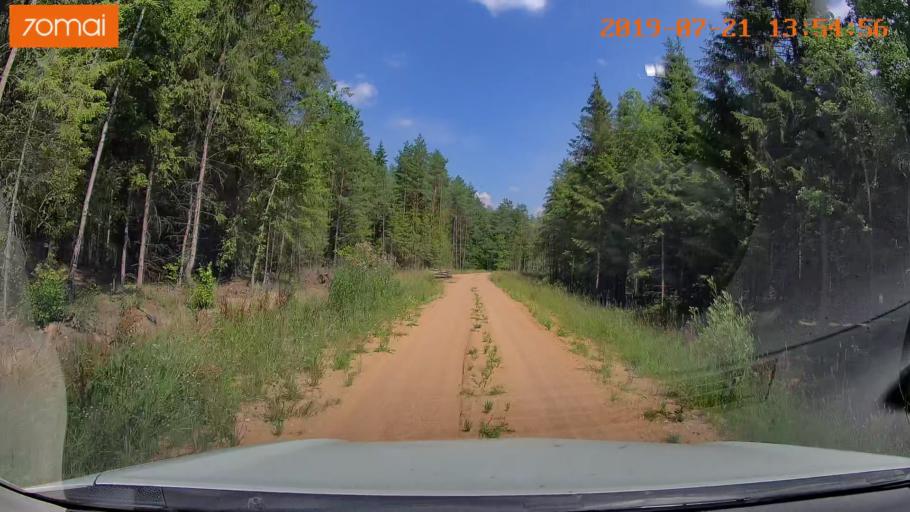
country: BY
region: Grodnenskaya
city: Lyubcha
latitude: 53.7785
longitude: 26.0797
